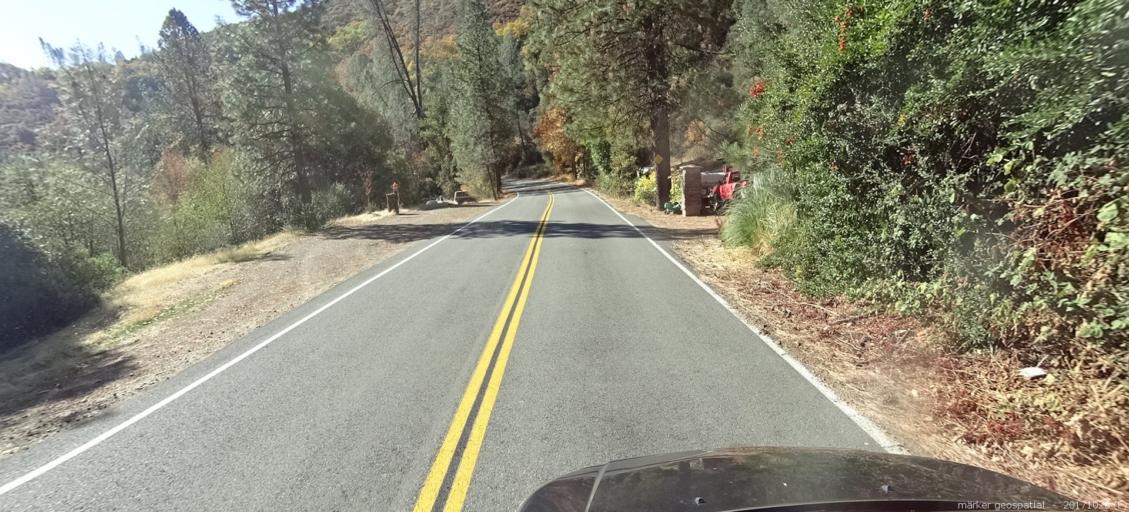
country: US
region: California
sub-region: Trinity County
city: Lewiston
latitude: 40.7344
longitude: -122.6262
